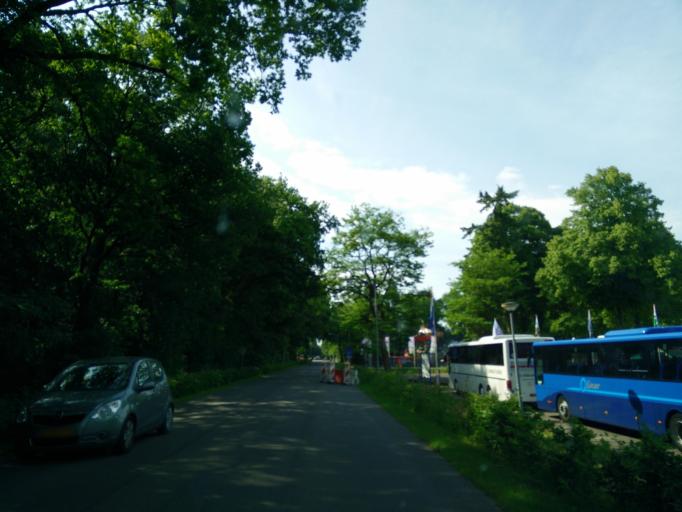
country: NL
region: Drenthe
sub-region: Gemeente Borger-Odoorn
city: Borger
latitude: 52.9578
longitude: 6.7887
